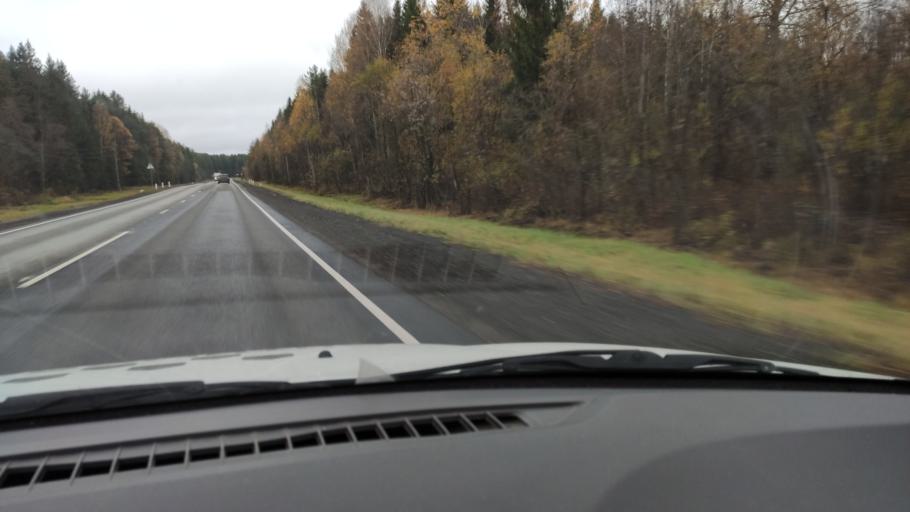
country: RU
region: Kirov
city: Belaya Kholunitsa
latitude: 58.8841
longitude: 50.8730
